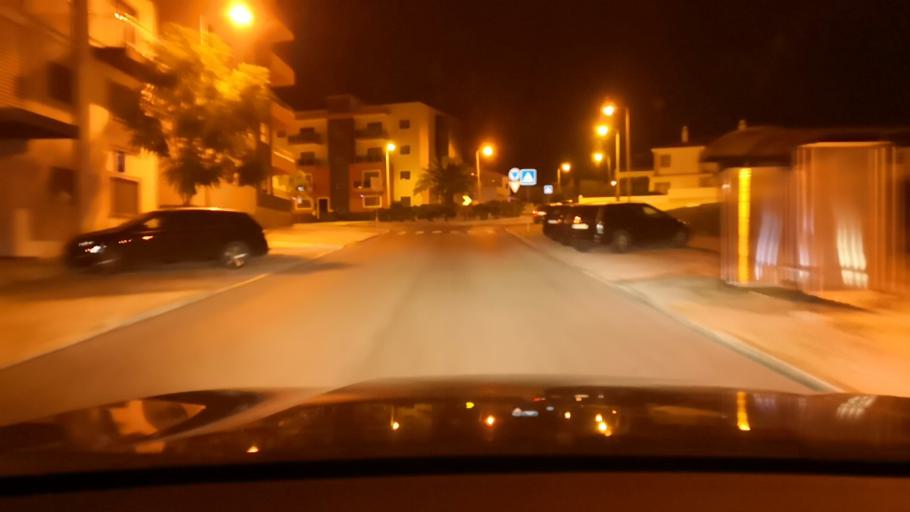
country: PT
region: Setubal
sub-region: Setubal
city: Setubal
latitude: 38.5429
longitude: -8.8560
